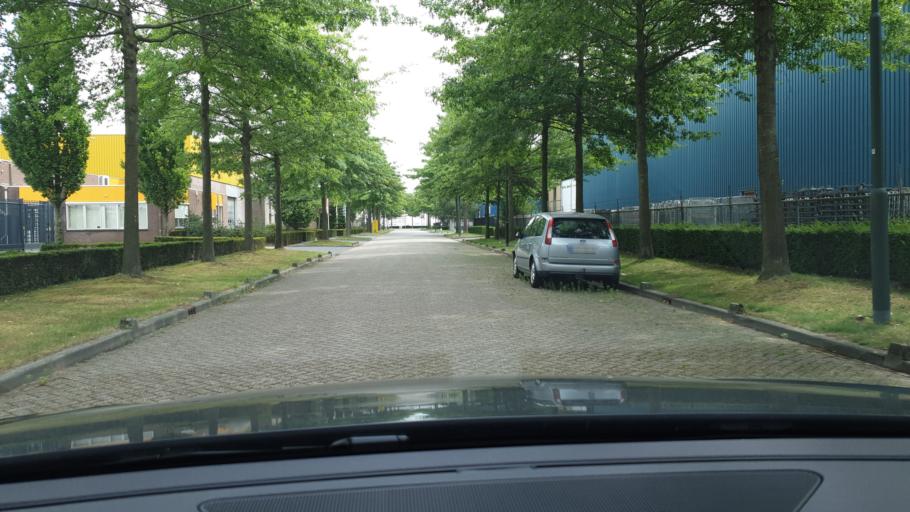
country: NL
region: North Brabant
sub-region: Gemeente Son en Breugel
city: Son
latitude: 51.4982
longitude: 5.4897
